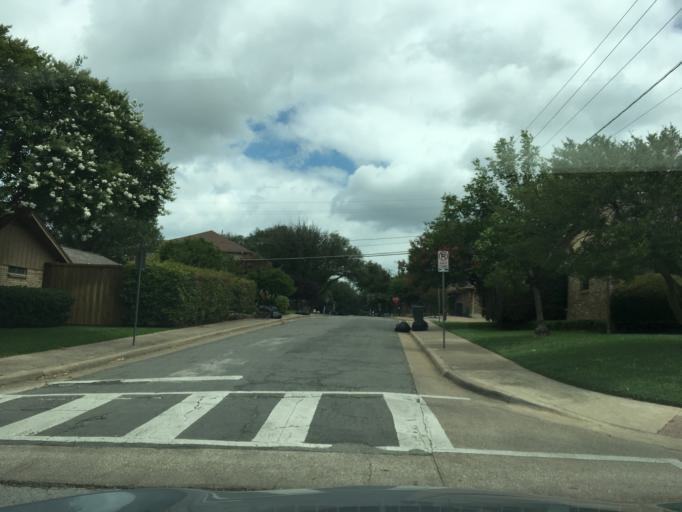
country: US
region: Texas
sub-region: Dallas County
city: Richardson
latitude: 32.8961
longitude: -96.7443
